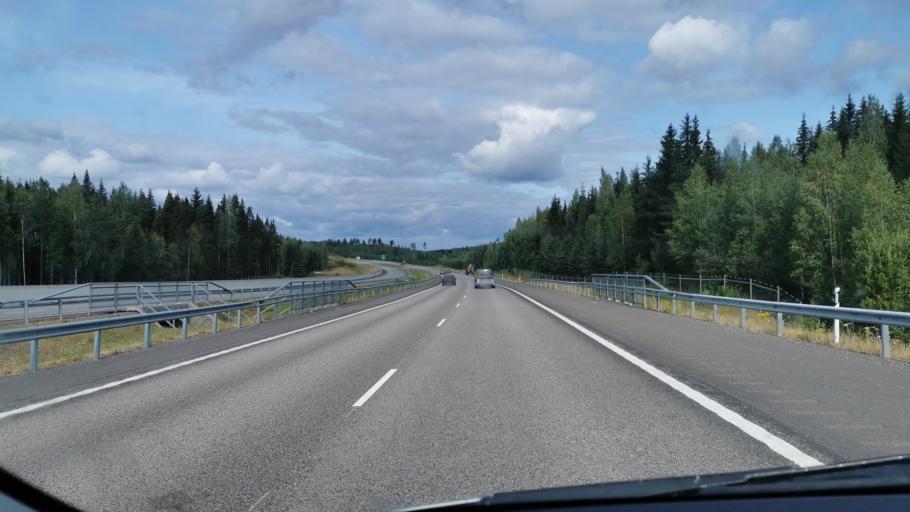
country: FI
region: Uusimaa
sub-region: Loviisa
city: Perna
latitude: 60.4868
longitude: 26.0131
